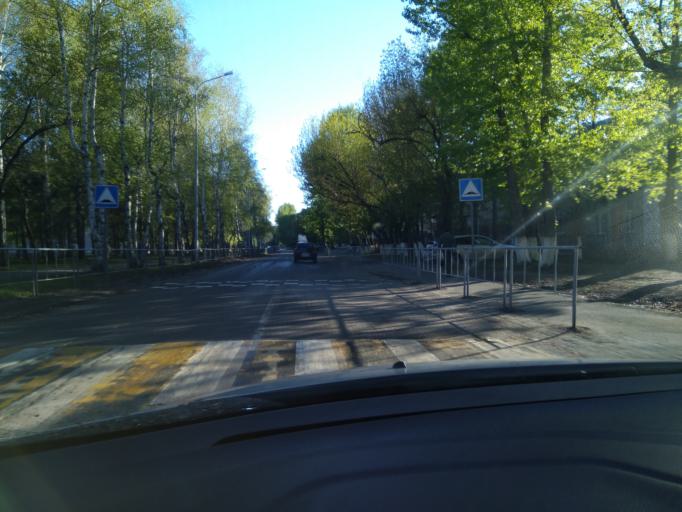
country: RU
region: Tjumen
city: Tyumen
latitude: 57.1327
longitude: 65.5899
